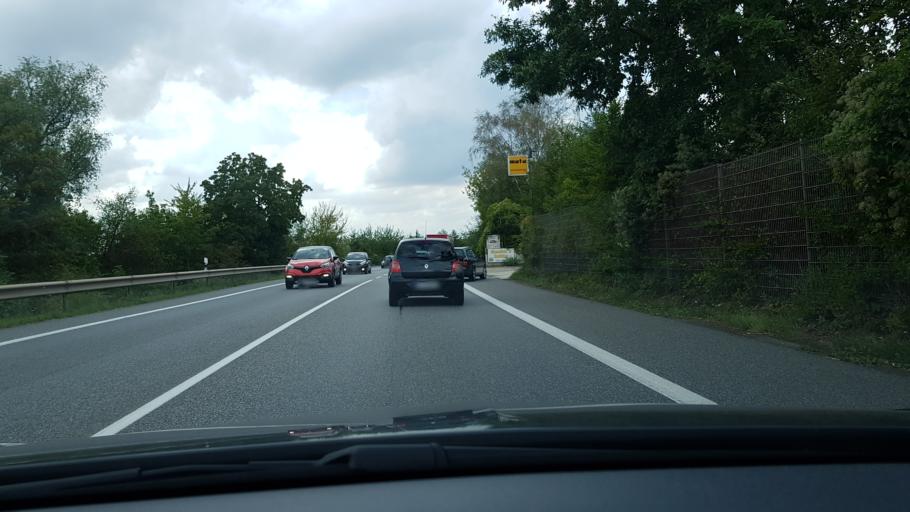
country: DE
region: Rheinland-Pfalz
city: Plaidt
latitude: 50.3988
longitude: 7.3983
